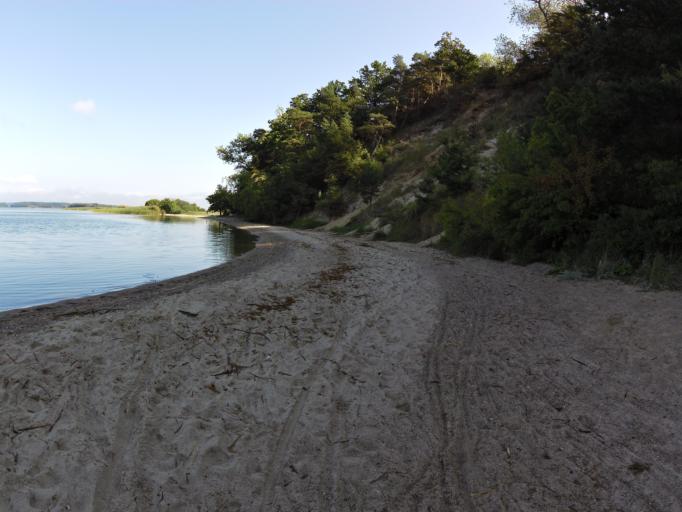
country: DE
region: Mecklenburg-Vorpommern
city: Loddin
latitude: 53.9690
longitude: 14.0441
